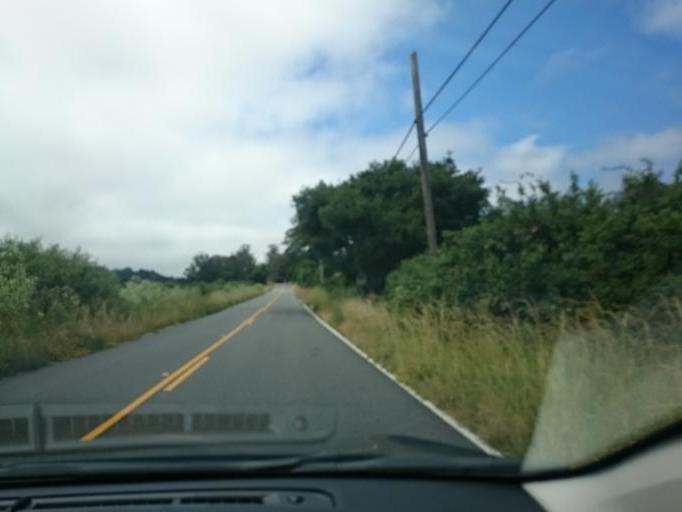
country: US
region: California
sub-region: Marin County
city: Lagunitas-Forest Knolls
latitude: 37.9655
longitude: -122.7237
